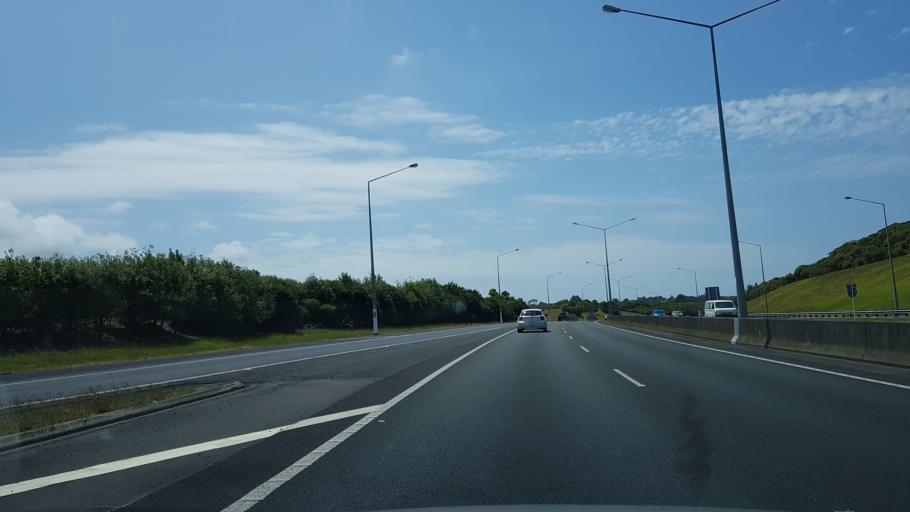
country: NZ
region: Auckland
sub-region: Auckland
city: Rothesay Bay
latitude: -36.7698
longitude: 174.6867
